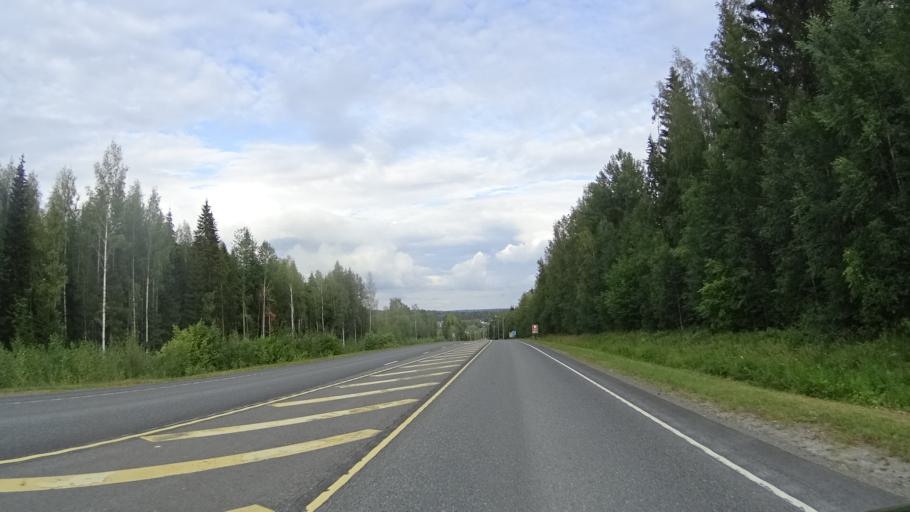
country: FI
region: Haeme
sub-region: Haemeenlinna
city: Parola
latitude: 61.0255
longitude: 24.3092
